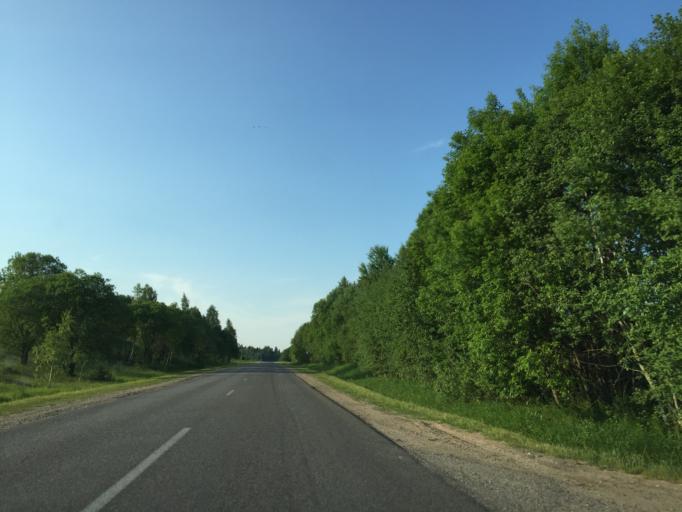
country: LT
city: Plateliai
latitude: 56.0543
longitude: 21.8194
